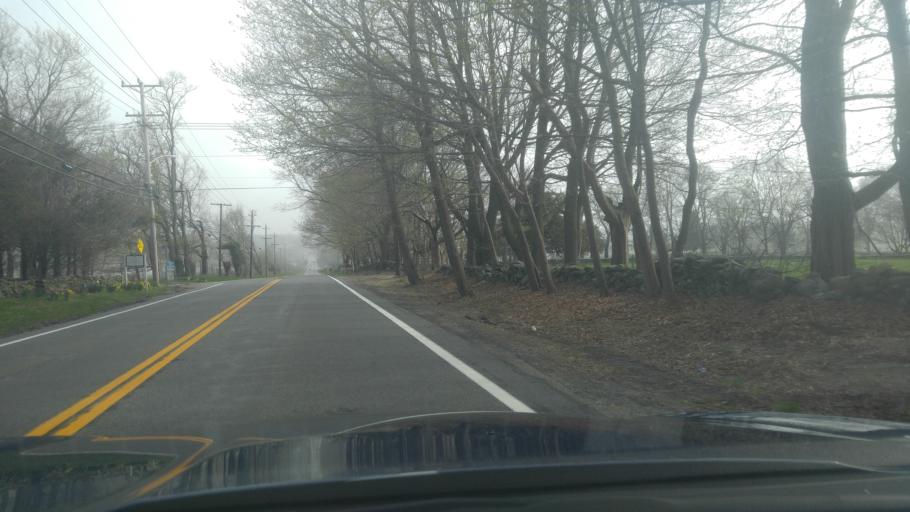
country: US
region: Rhode Island
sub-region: Newport County
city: Jamestown
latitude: 41.5145
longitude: -71.3749
